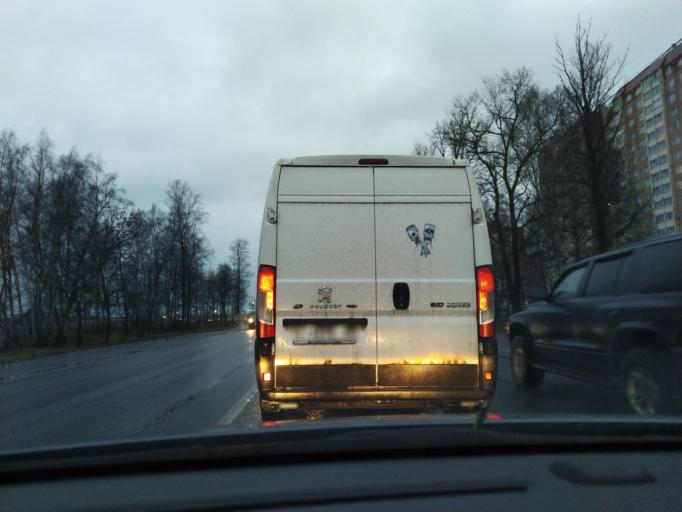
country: RU
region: St.-Petersburg
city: Gorelovo
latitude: 59.7896
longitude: 30.1445
